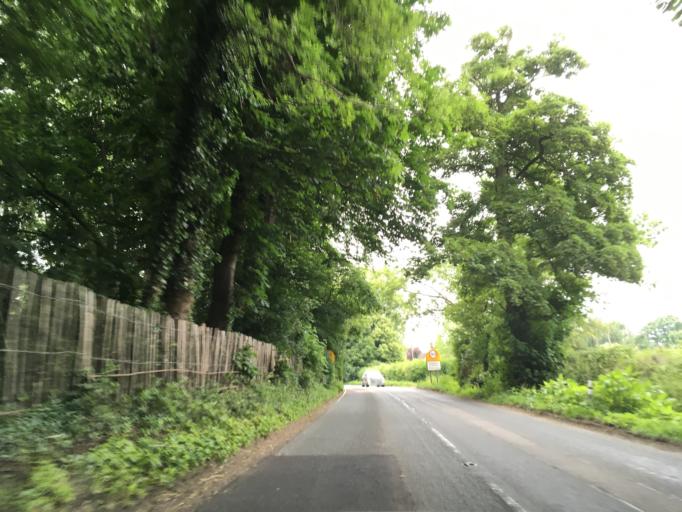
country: GB
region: England
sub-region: Gloucestershire
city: Stonehouse
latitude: 51.7703
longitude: -2.3598
